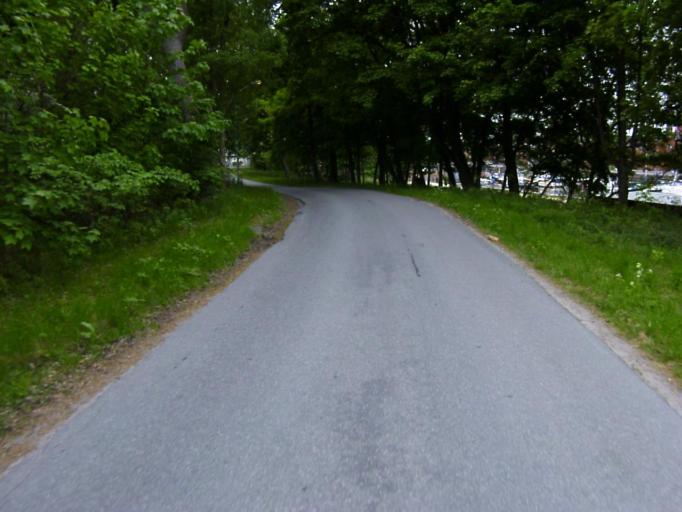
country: SE
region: Skane
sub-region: Kristianstads Kommun
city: Ahus
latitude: 55.9233
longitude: 14.3024
